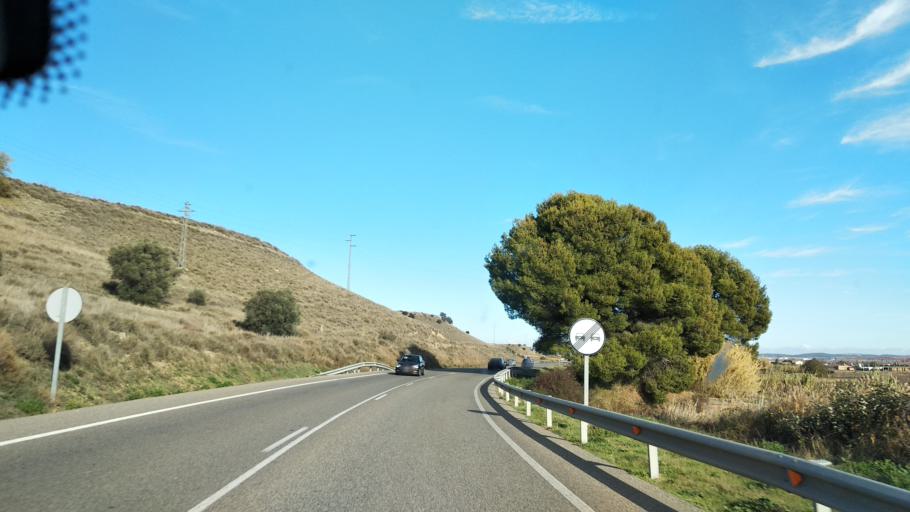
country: ES
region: Catalonia
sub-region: Provincia de Lleida
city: Vallfogona de Balaguer
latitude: 41.7626
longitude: 0.7775
